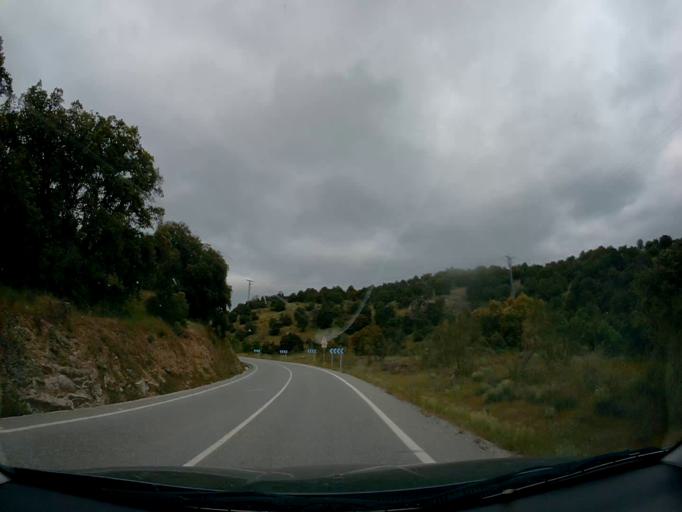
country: ES
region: Madrid
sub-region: Provincia de Madrid
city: Navalagamella
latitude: 40.4410
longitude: -4.1136
